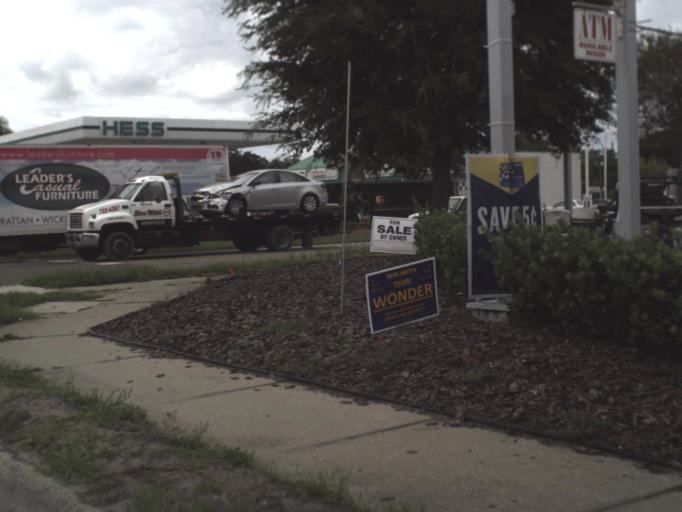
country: US
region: Florida
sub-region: Manatee County
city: Whitfield
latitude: 27.4229
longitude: -82.5756
